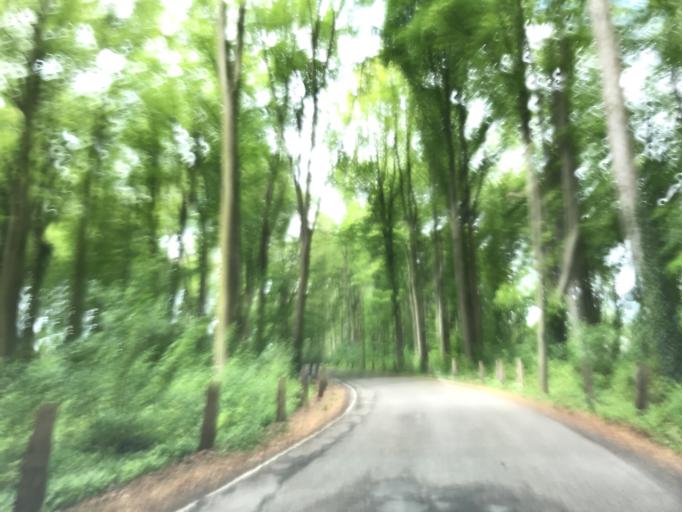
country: DE
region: North Rhine-Westphalia
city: Witten
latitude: 51.4791
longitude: 7.3708
